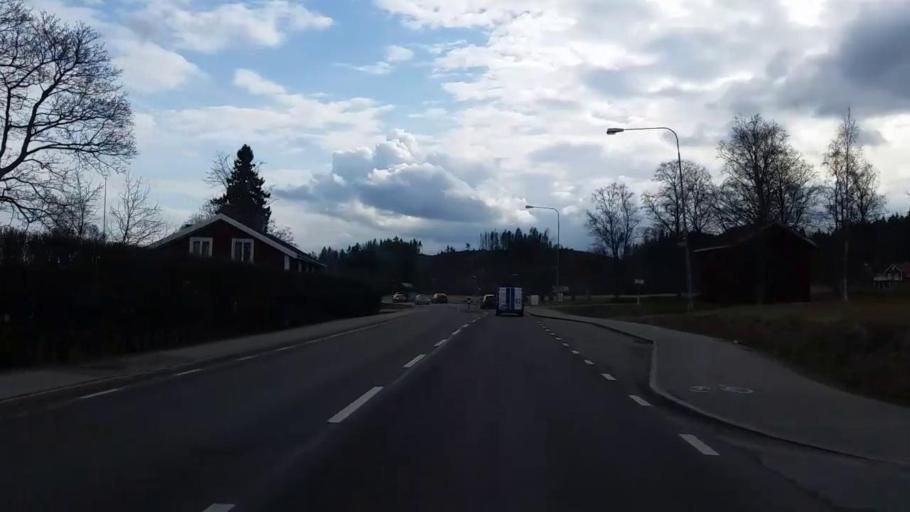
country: SE
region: Gaevleborg
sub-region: Ljusdals Kommun
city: Jaervsoe
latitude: 61.7076
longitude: 16.1634
